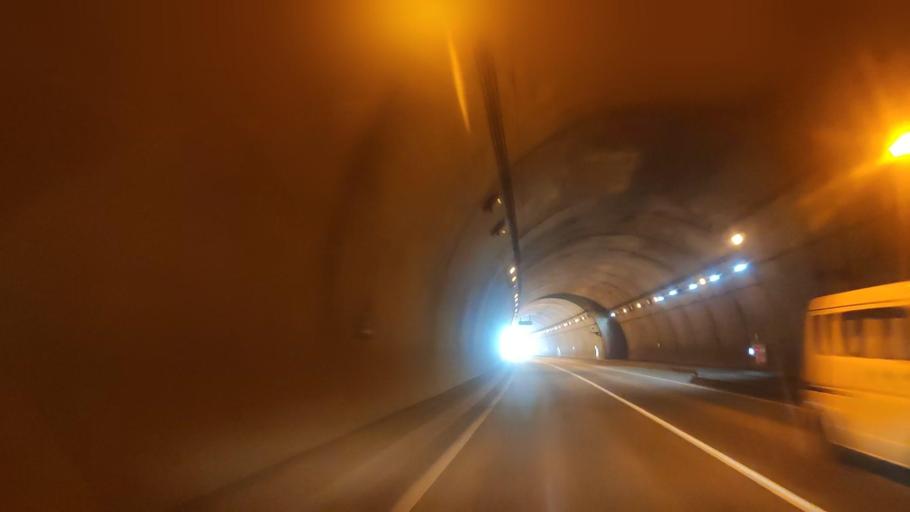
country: JP
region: Hokkaido
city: Date
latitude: 42.5681
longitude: 140.7955
